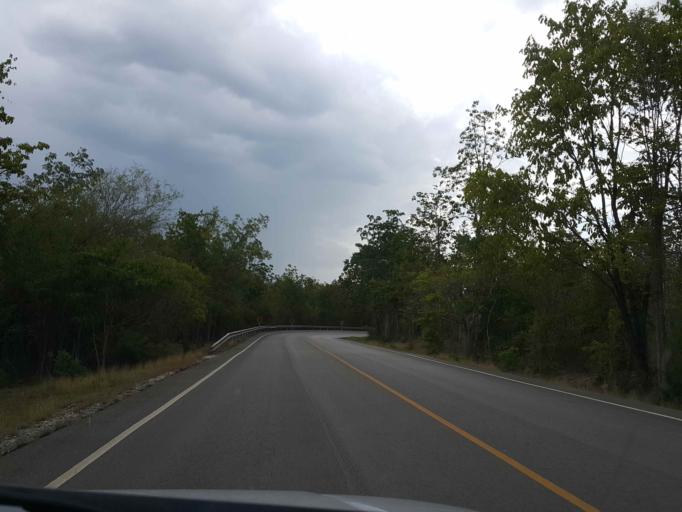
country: TH
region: Sukhothai
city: Thung Saliam
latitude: 17.3655
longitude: 99.4098
